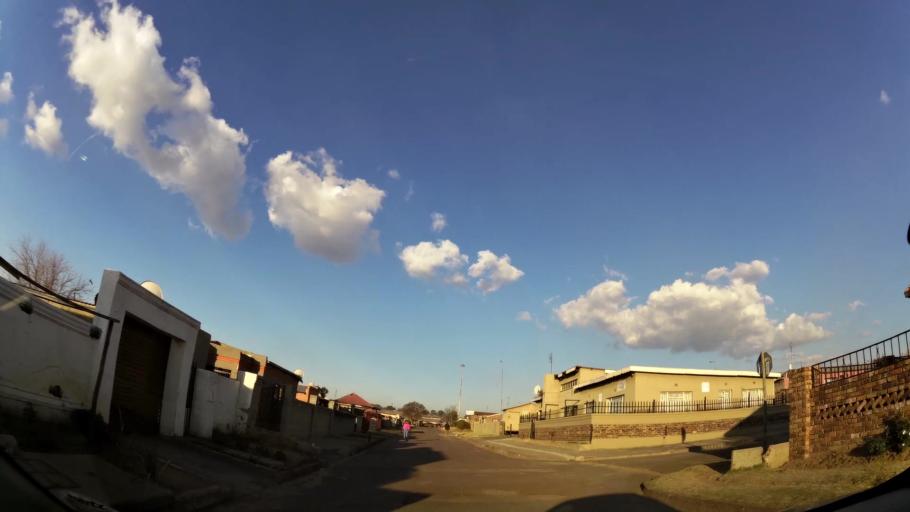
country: ZA
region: Mpumalanga
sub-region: Nkangala District Municipality
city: Witbank
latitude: -25.8768
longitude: 29.1913
